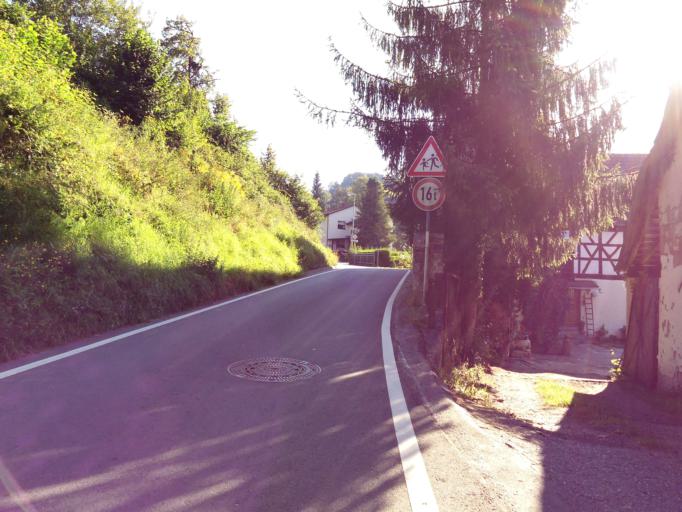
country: DE
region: Hesse
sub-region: Regierungsbezirk Darmstadt
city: Heppenheim an der Bergstrasse
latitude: 49.6670
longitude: 8.6854
